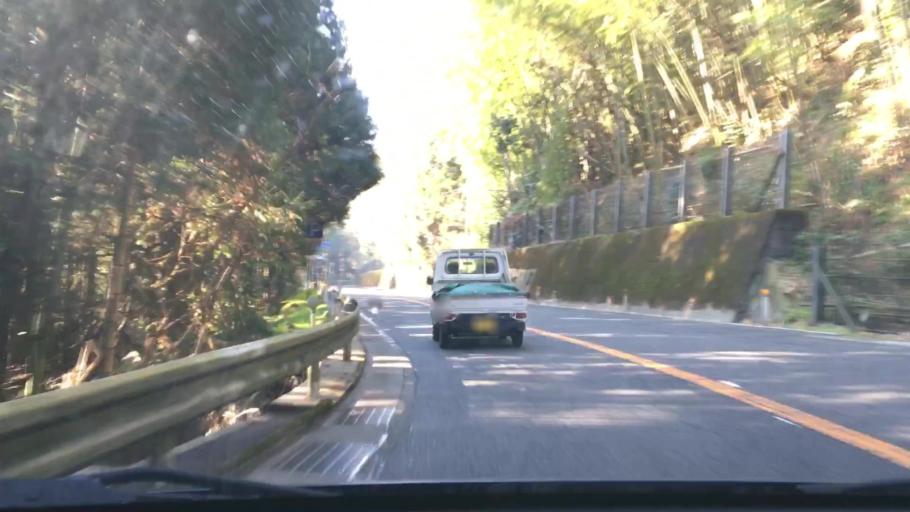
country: JP
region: Kagoshima
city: Sueyoshicho-ninokata
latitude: 31.6644
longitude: 130.9045
